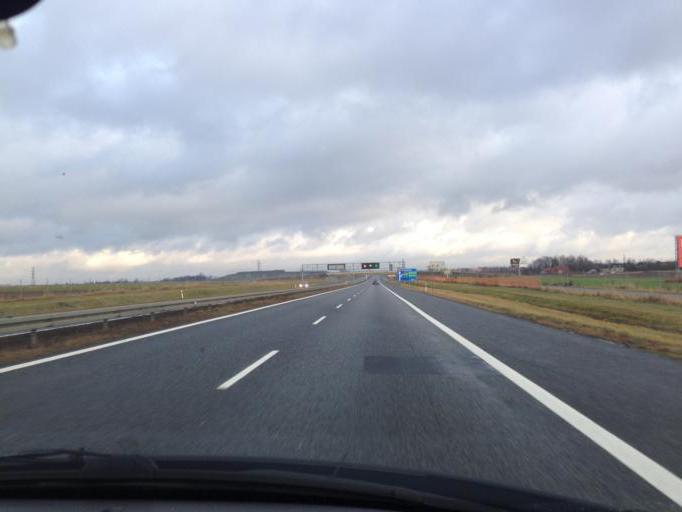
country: PL
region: Silesian Voivodeship
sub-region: Powiat gliwicki
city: Zernica
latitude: 50.2623
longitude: 18.6316
